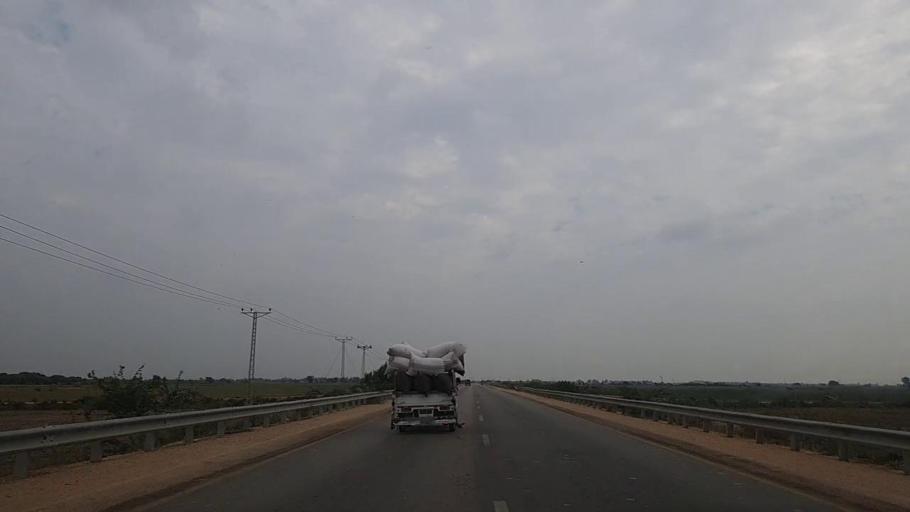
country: PK
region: Sindh
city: Thatta
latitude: 24.6166
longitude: 68.0658
